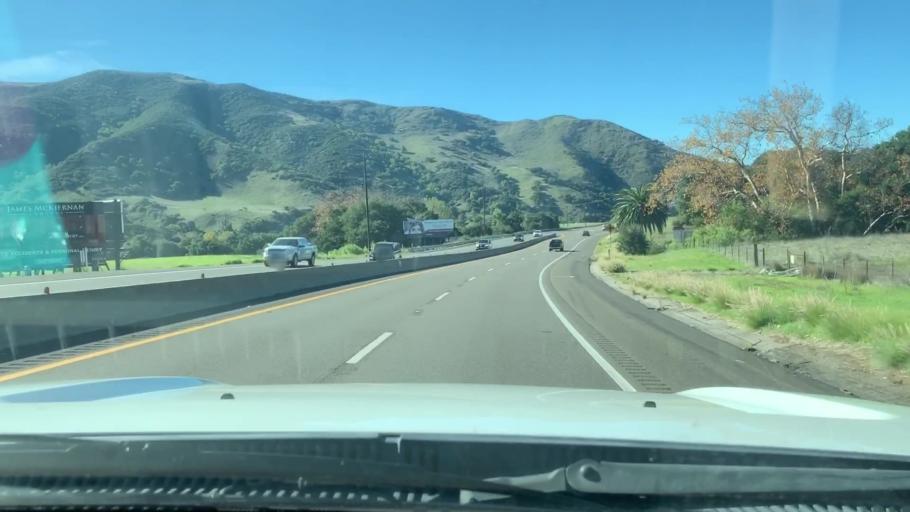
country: US
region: California
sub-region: San Luis Obispo County
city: San Luis Obispo
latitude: 35.2980
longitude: -120.6269
